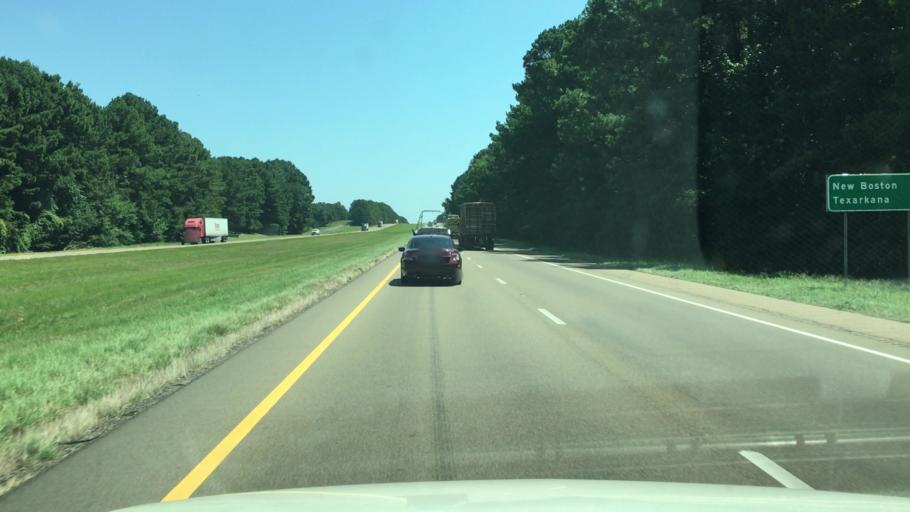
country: US
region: Texas
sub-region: Bowie County
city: De Kalb
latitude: 33.3763
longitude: -94.6177
